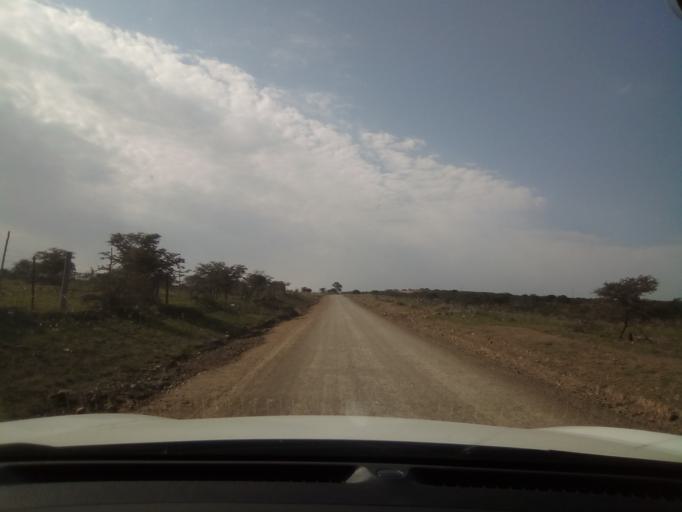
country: ZA
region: Eastern Cape
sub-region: Buffalo City Metropolitan Municipality
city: Bhisho
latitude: -32.9878
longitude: 27.2452
